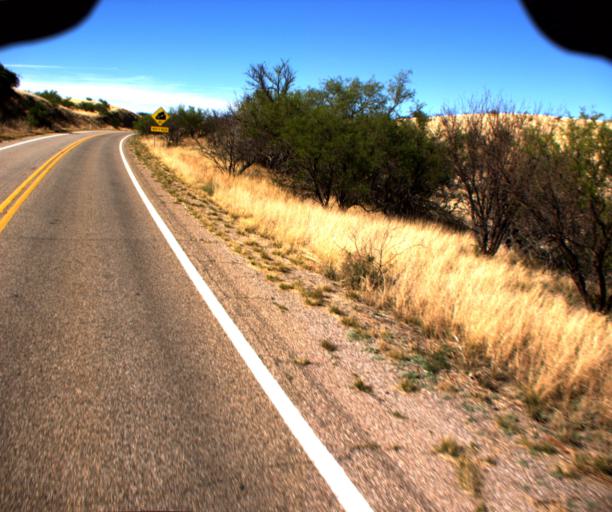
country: US
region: Arizona
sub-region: Pima County
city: Corona de Tucson
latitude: 31.8132
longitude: -110.7119
